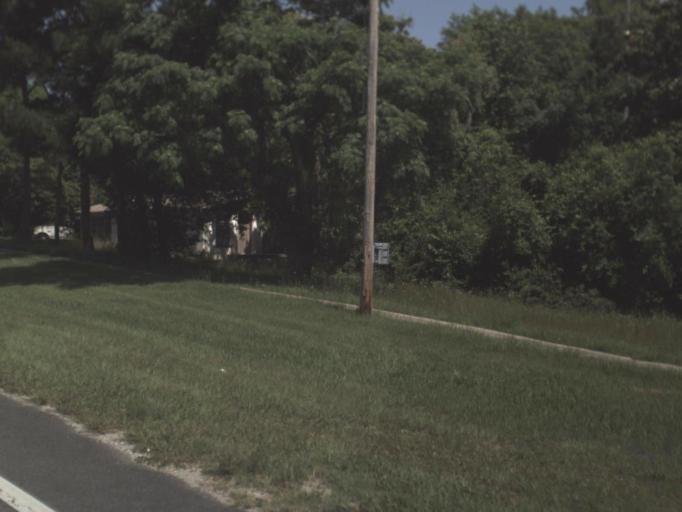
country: US
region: Florida
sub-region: Clay County
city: Green Cove Springs
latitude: 29.9838
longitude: -81.7212
